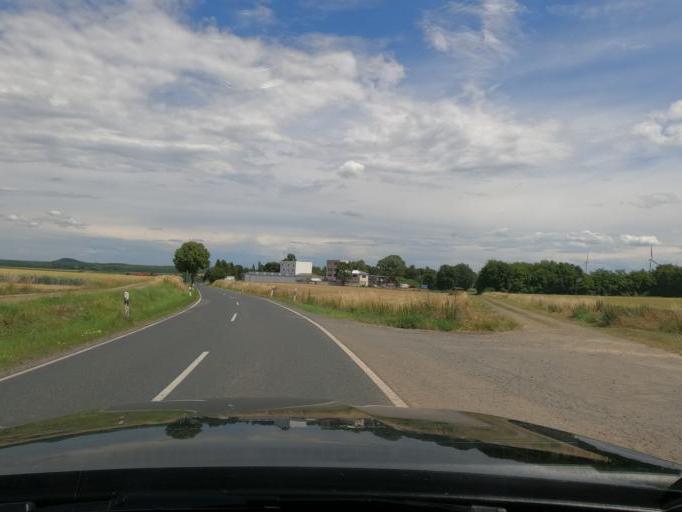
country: DE
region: Lower Saxony
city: Sohlde
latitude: 52.1850
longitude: 10.2660
